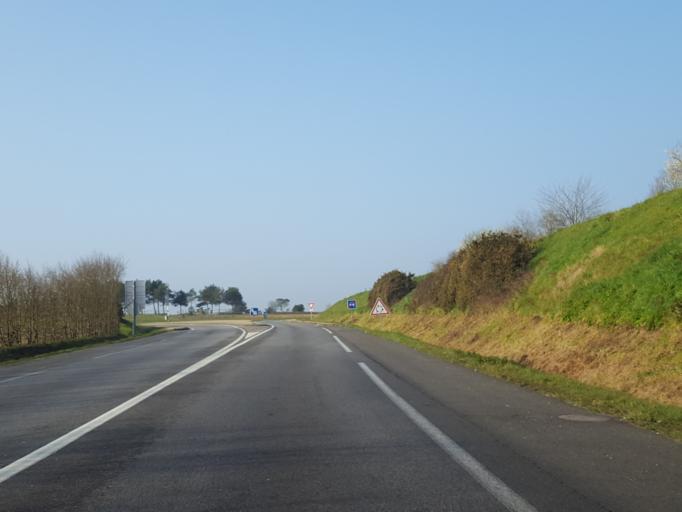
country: FR
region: Pays de la Loire
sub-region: Departement de la Vendee
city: La Roche-sur-Yon
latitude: 46.6669
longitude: -1.4634
